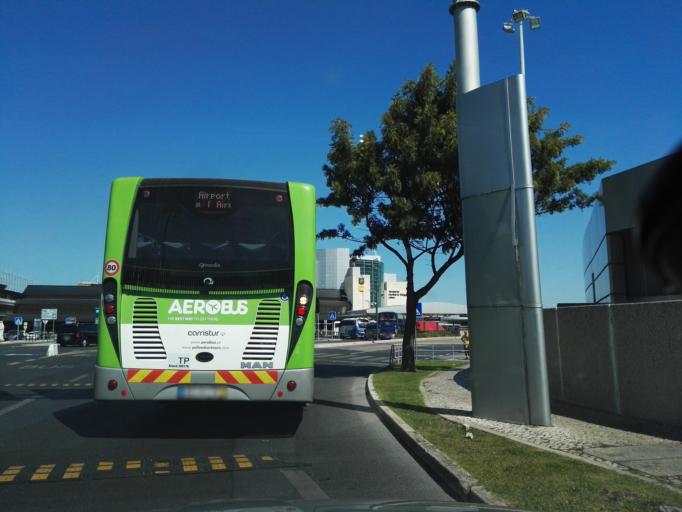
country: PT
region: Lisbon
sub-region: Loures
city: Moscavide
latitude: 38.7674
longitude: -9.1289
